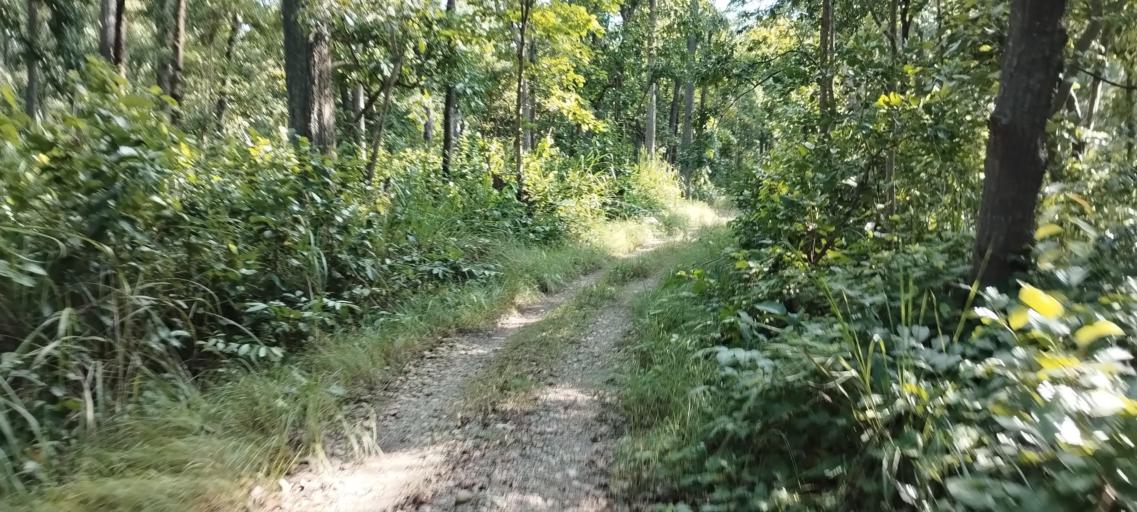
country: NP
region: Far Western
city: Tikapur
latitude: 28.5293
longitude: 81.2829
